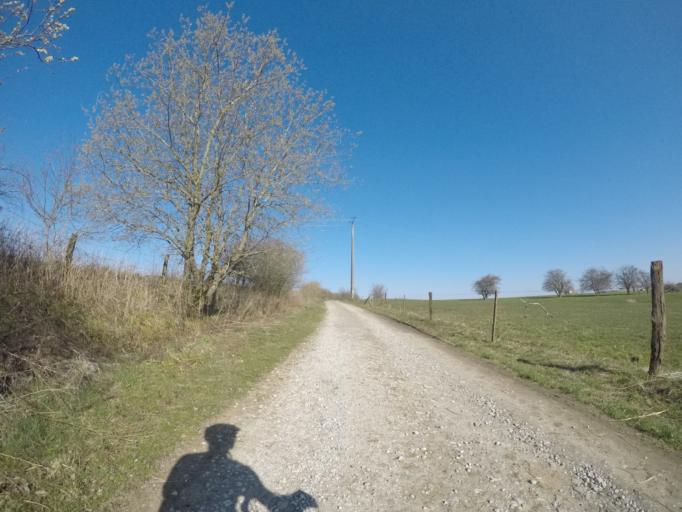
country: BE
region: Wallonia
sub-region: Province du Luxembourg
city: Etalle
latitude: 49.7094
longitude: 5.5778
